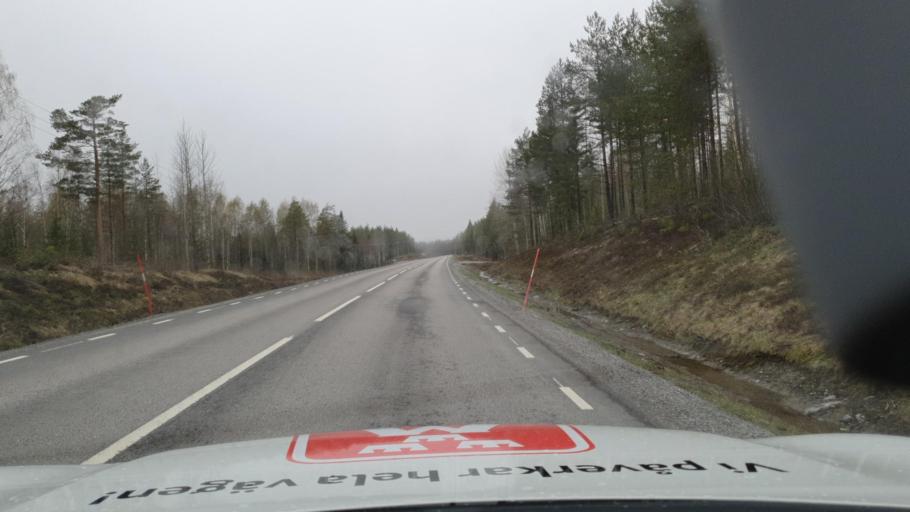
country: SE
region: Vaesterbotten
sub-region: Umea Kommun
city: Hoernefors
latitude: 63.7723
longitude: 19.9702
